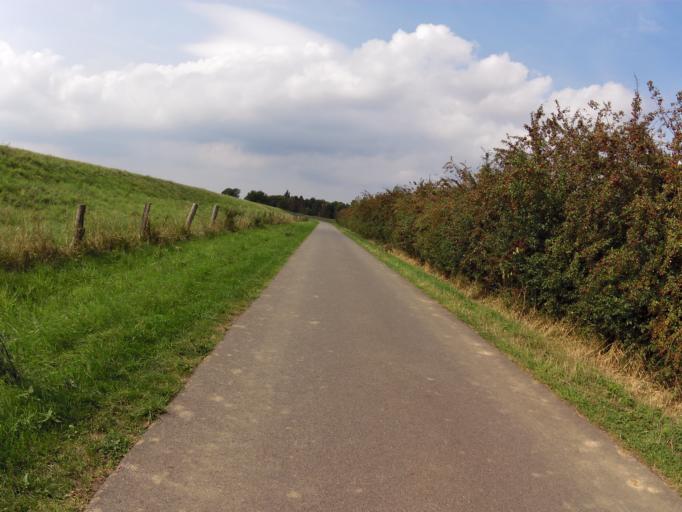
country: DE
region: Lower Saxony
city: Hilgermissen
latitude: 52.8919
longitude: 9.1717
